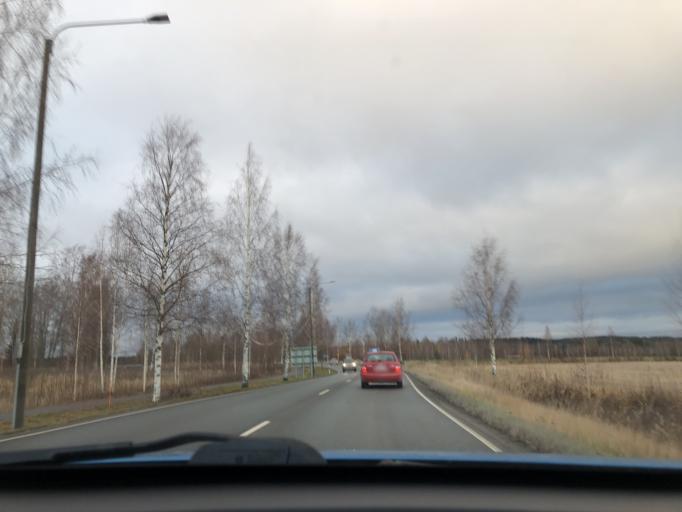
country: FI
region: Pirkanmaa
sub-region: Tampere
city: Kangasala
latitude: 61.4730
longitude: 24.0575
